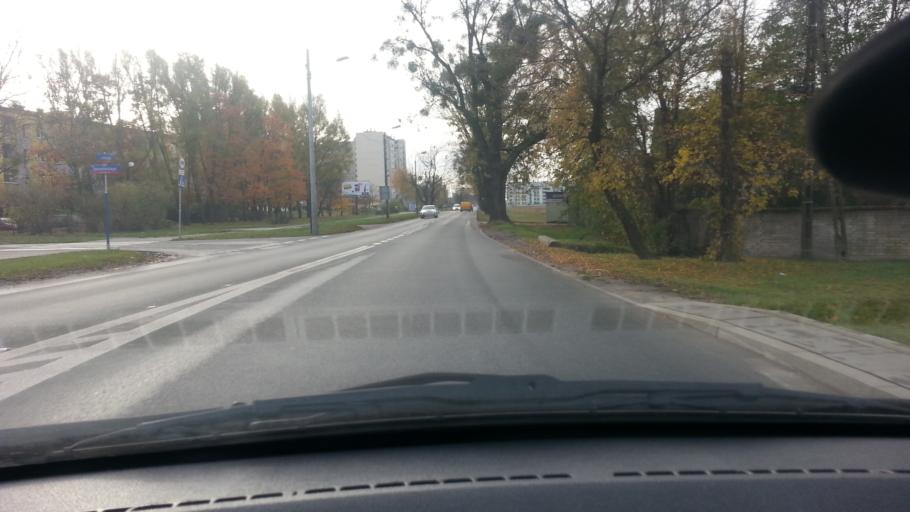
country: PL
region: Masovian Voivodeship
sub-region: Warszawa
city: Bemowo
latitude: 52.2383
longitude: 20.8964
